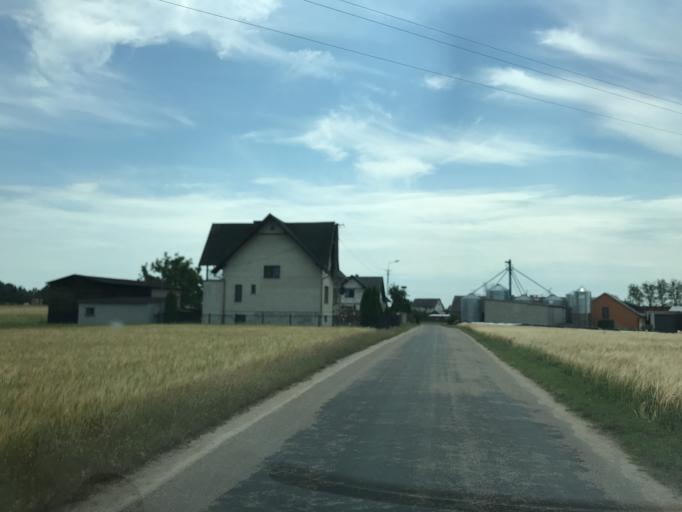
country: PL
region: Kujawsko-Pomorskie
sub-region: Powiat brodnicki
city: Bartniczka
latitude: 53.2523
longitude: 19.5662
